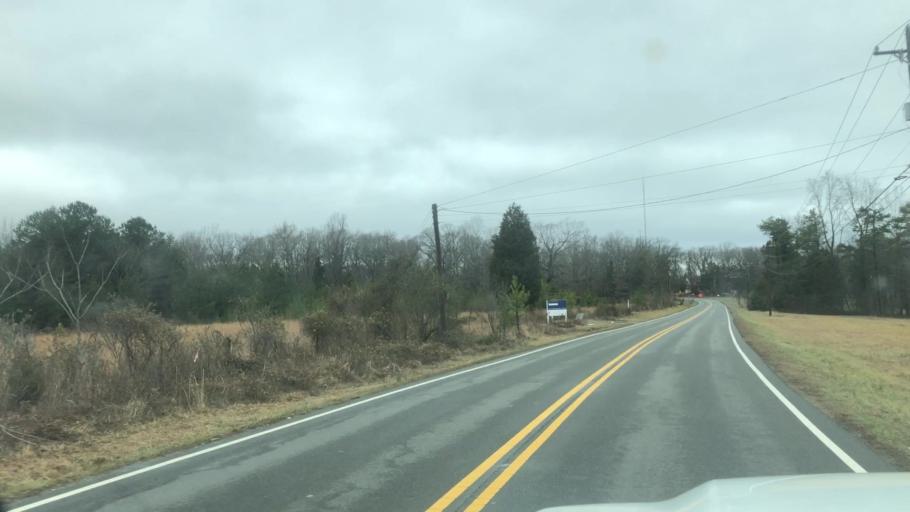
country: US
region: North Carolina
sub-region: Mecklenburg County
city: Mint Hill
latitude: 35.2378
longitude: -80.6709
